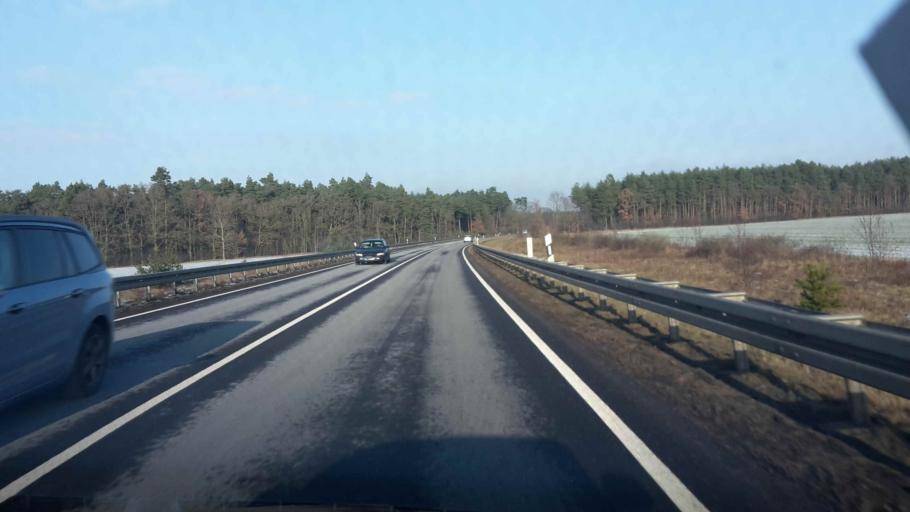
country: DE
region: Brandenburg
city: Weisen
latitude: 53.0270
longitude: 11.7746
